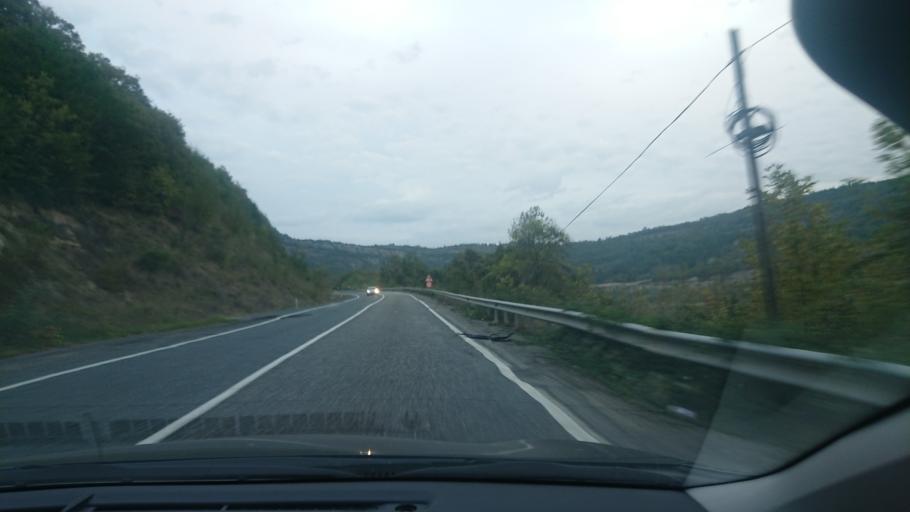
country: TR
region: Zonguldak
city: Gokcebey
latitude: 41.2815
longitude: 32.1611
